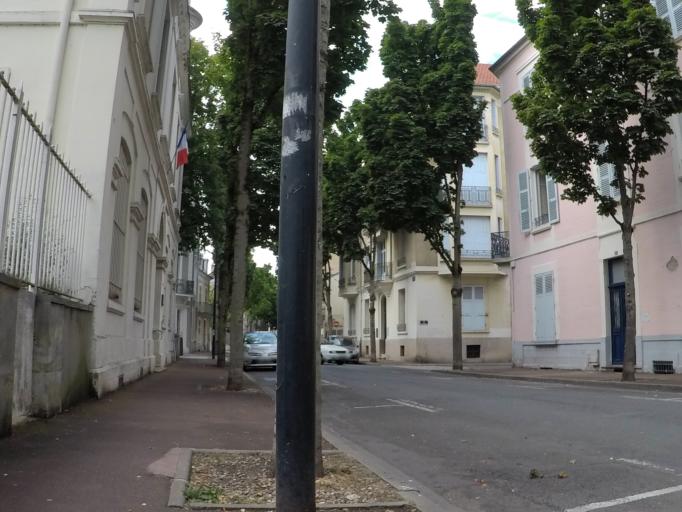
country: FR
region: Auvergne
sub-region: Departement de l'Allier
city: Vichy
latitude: 46.1234
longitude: 3.4254
